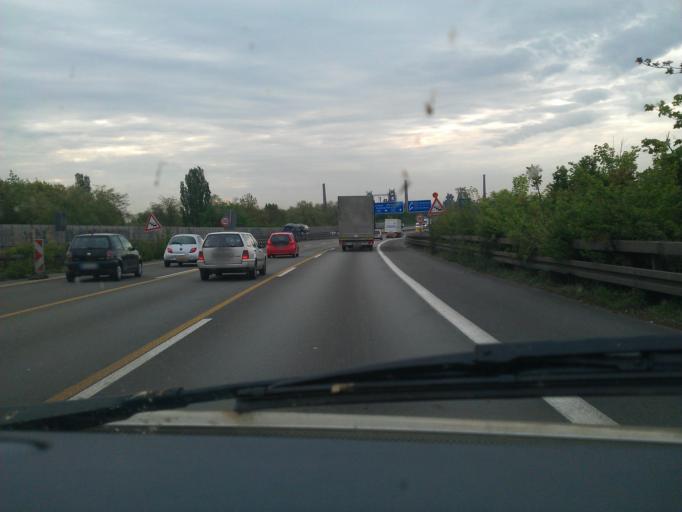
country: DE
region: North Rhine-Westphalia
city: Meiderich
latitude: 51.4862
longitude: 6.7622
